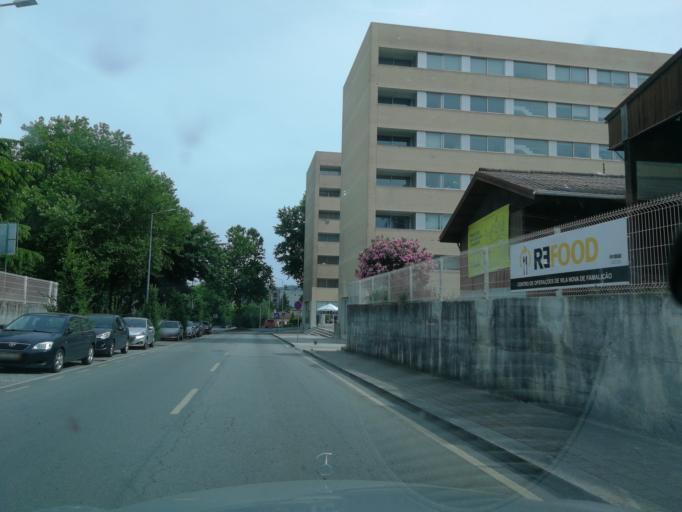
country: PT
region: Braga
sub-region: Vila Nova de Famalicao
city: Calendario
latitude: 41.4067
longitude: -8.5282
